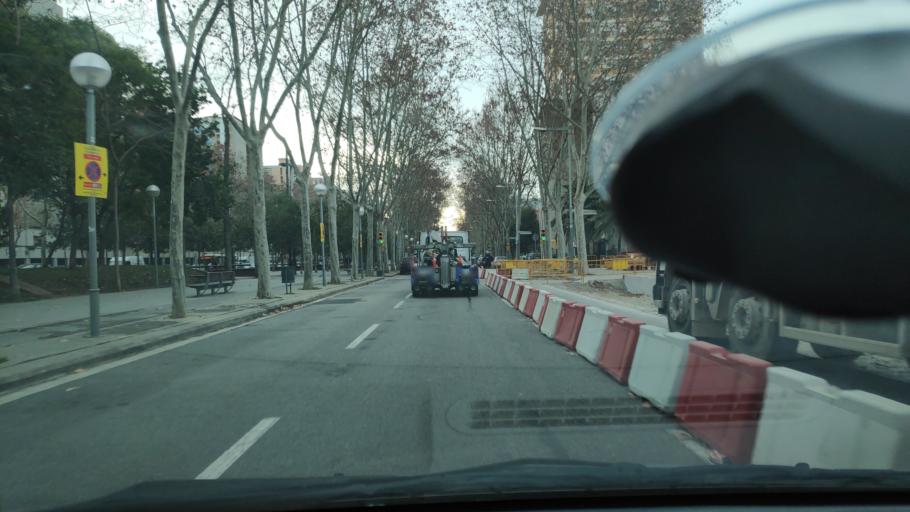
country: ES
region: Catalonia
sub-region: Provincia de Barcelona
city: Sant Marti
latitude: 41.4171
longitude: 2.2112
